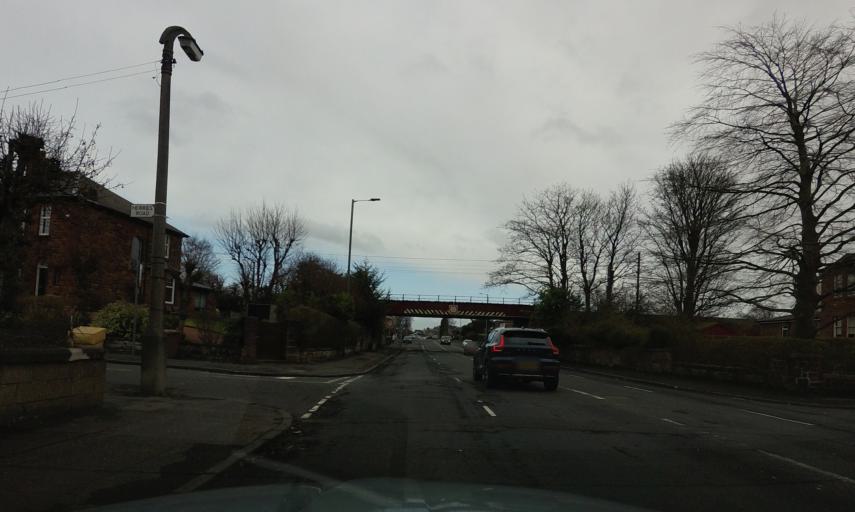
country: GB
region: Scotland
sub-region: East Renfrewshire
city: Giffnock
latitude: 55.8346
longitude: -4.2948
